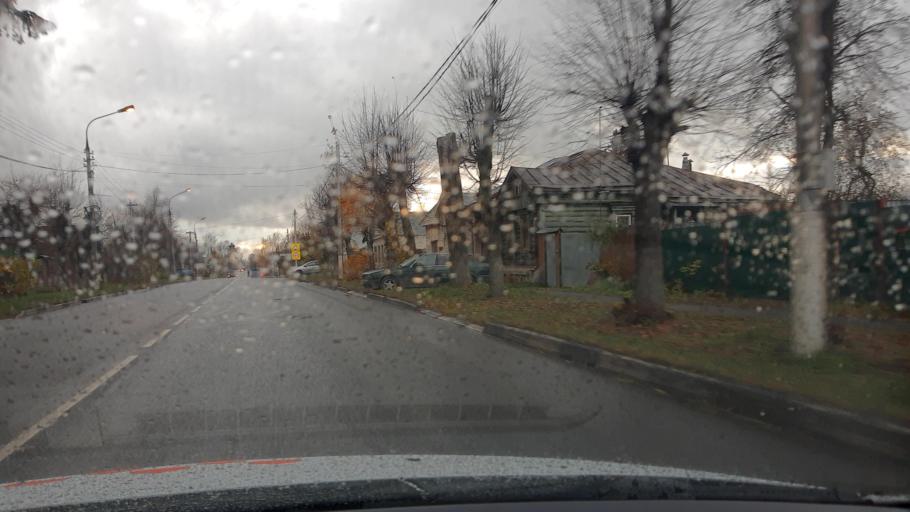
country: RU
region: Moskovskaya
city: Noginsk
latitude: 55.8527
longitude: 38.4255
